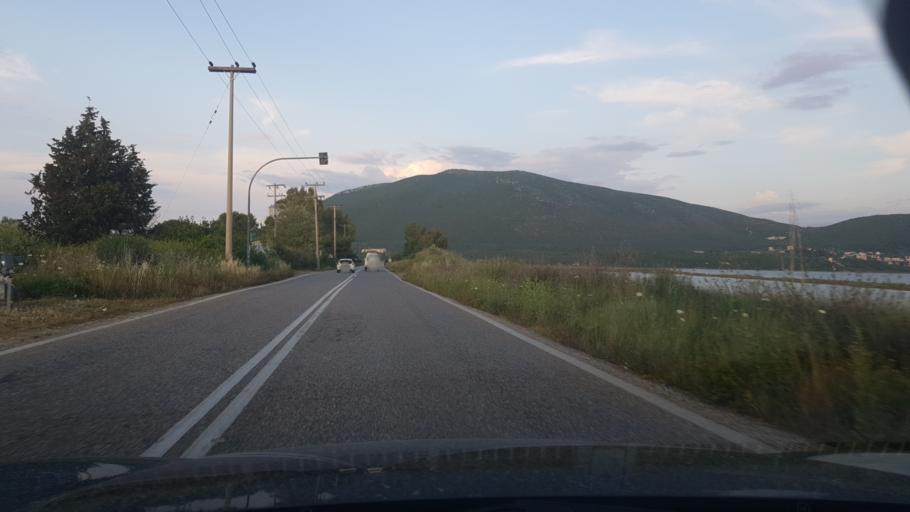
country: GR
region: Ionian Islands
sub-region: Lefkada
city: Lefkada
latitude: 38.8430
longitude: 20.7217
